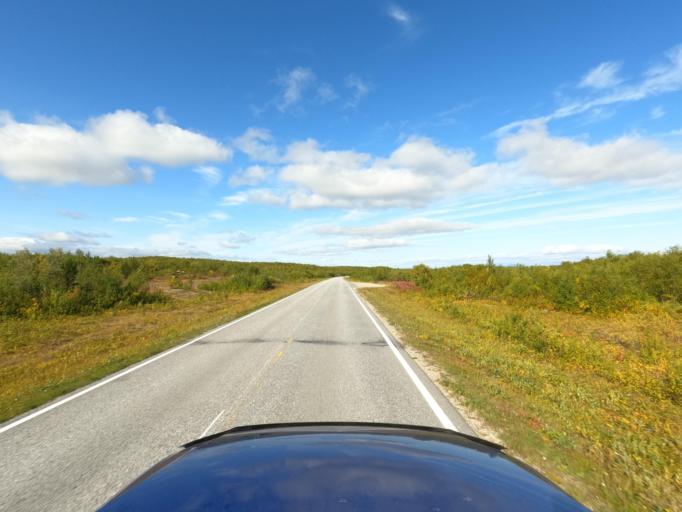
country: NO
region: Finnmark Fylke
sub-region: Karasjok
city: Karasjohka
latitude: 69.5929
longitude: 25.3346
